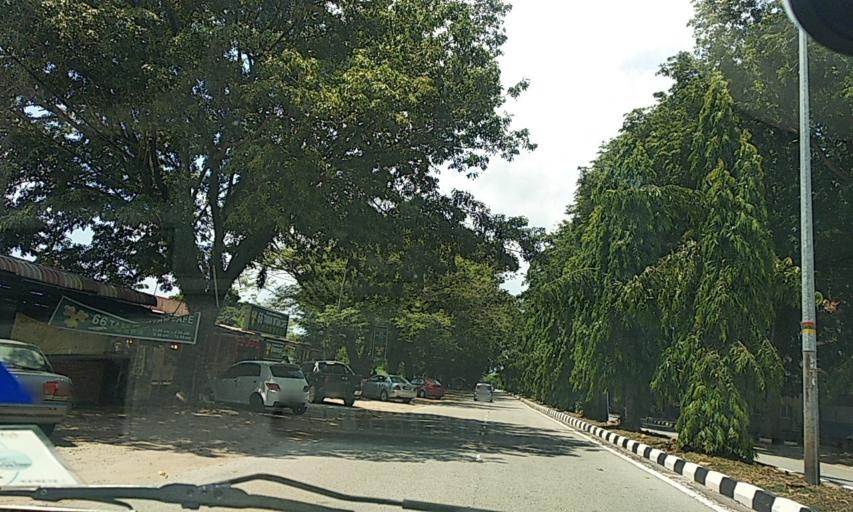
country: MY
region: Kedah
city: Sungai Petani
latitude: 5.6354
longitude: 100.4769
